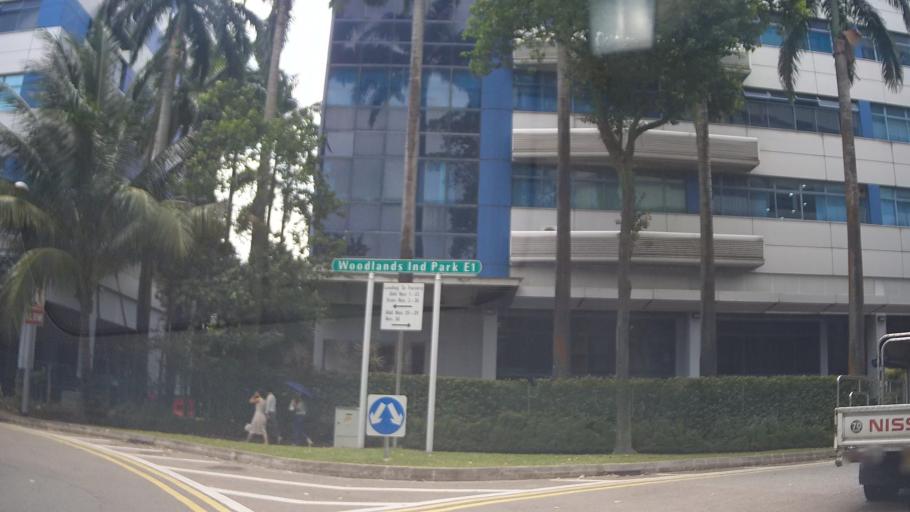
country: MY
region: Johor
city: Johor Bahru
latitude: 1.4543
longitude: 103.7975
